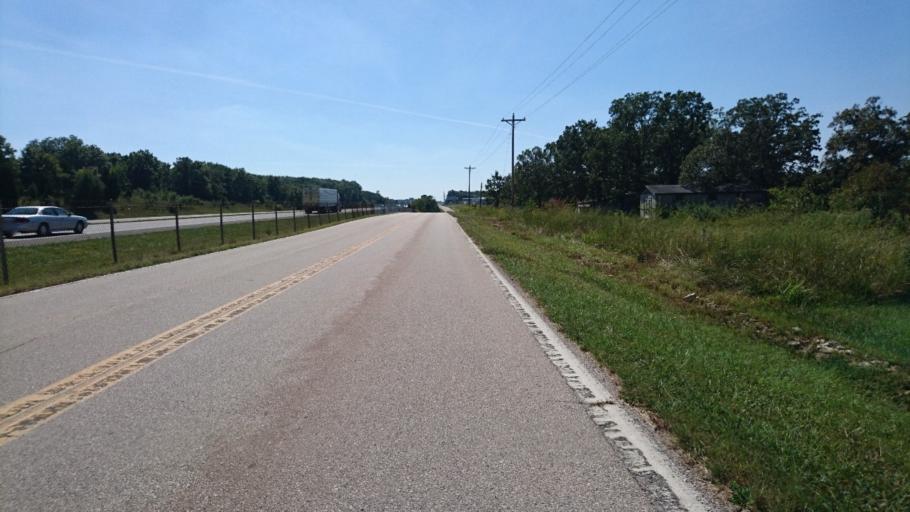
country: US
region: Missouri
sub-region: Franklin County
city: Sullivan
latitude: 38.2428
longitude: -91.1407
